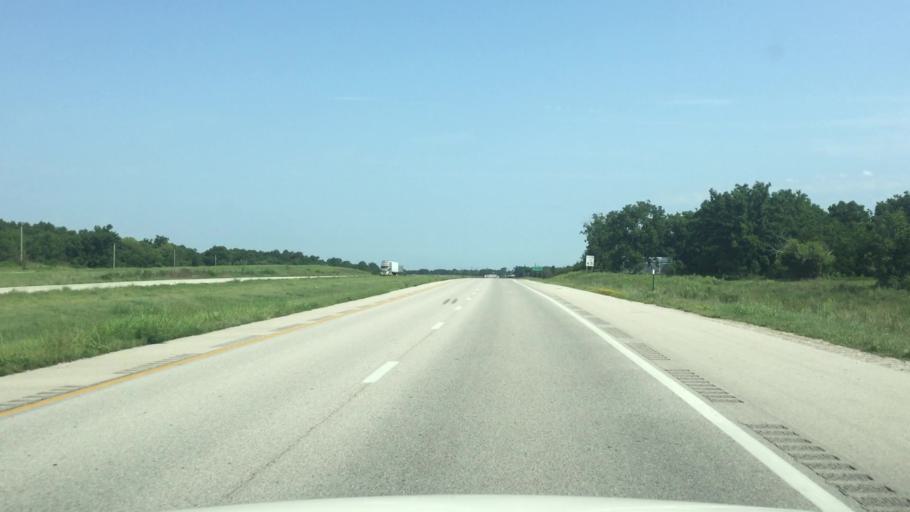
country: US
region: Kansas
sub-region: Montgomery County
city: Coffeyville
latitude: 37.0540
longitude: -95.5812
